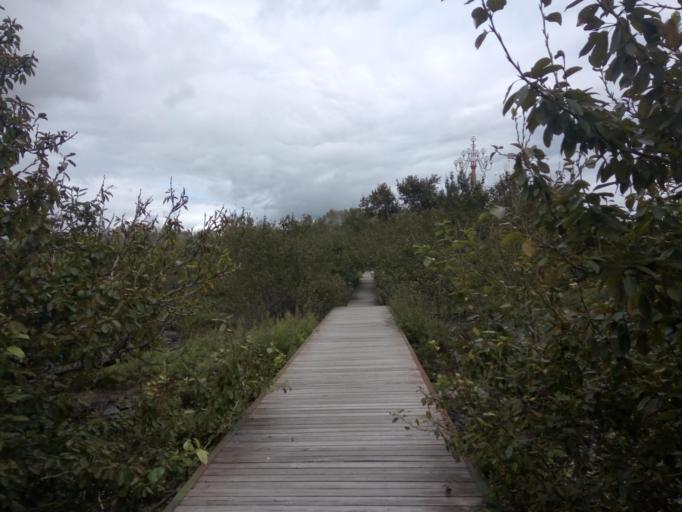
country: CN
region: Heilongjiang Sheng
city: Erjing
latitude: 48.6507
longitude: 126.1540
